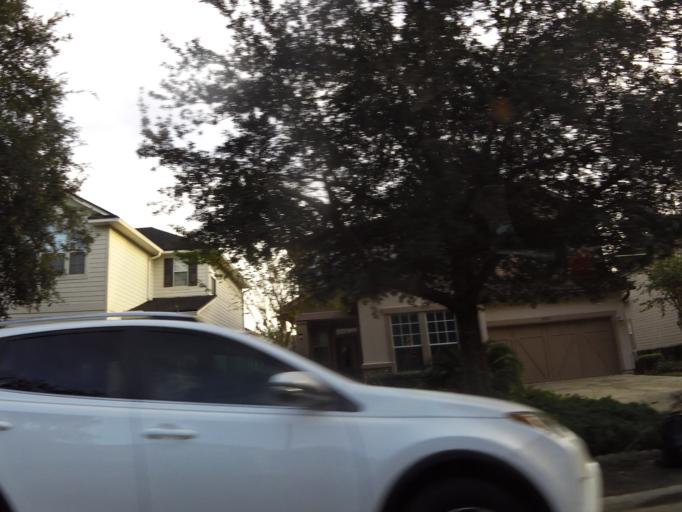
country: US
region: Florida
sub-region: Saint Johns County
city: Fruit Cove
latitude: 30.1509
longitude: -81.5447
